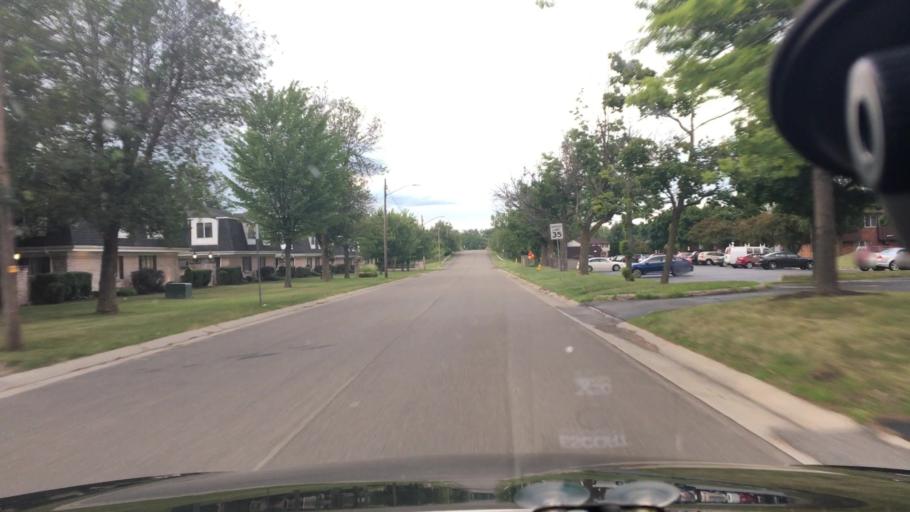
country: US
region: New York
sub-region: Erie County
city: West Seneca
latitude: 42.8401
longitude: -78.7648
